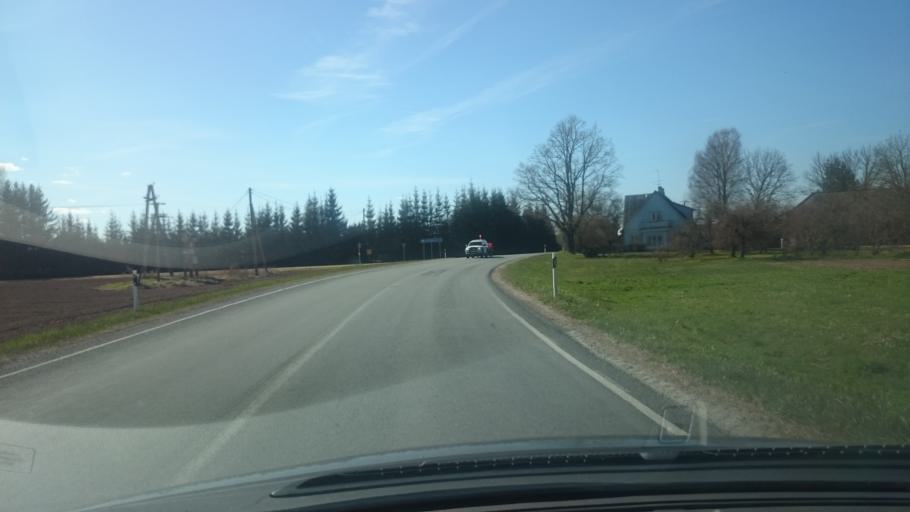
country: EE
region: Polvamaa
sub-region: Polva linn
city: Polva
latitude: 58.2256
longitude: 27.0312
